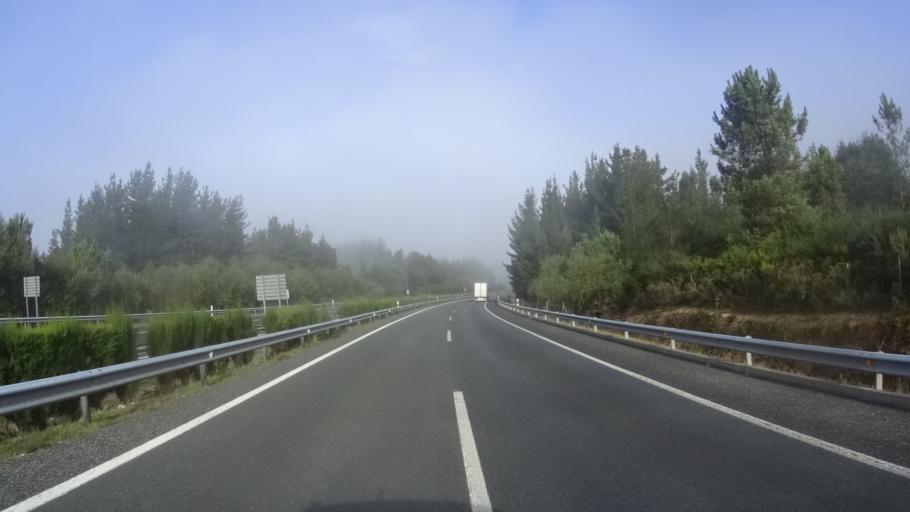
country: ES
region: Galicia
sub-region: Provincia de Lugo
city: Lancara
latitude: 42.9208
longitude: -7.3523
